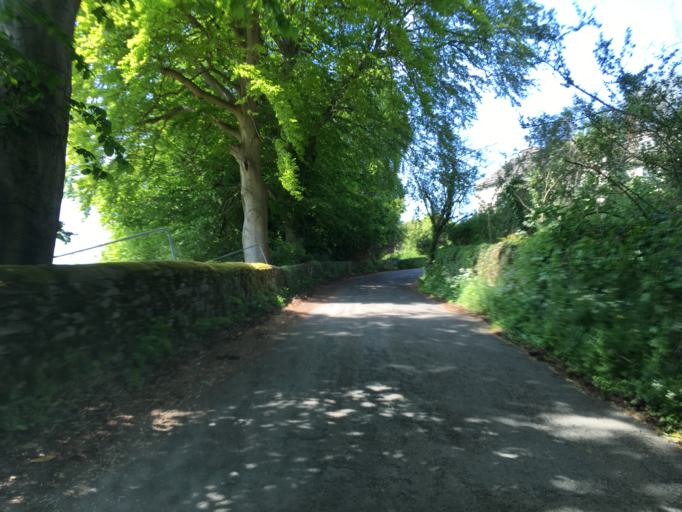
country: GB
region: England
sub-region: Gloucestershire
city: Minchinhampton
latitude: 51.6941
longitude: -2.1946
